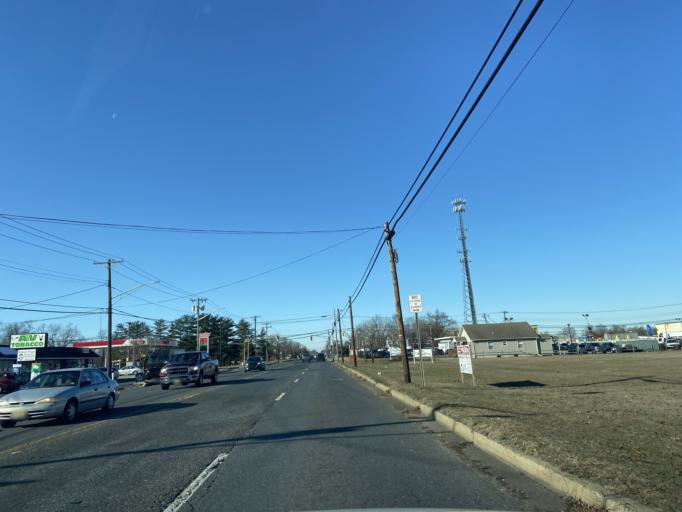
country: US
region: New Jersey
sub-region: Cumberland County
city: Vineland
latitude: 39.4878
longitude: -75.0601
